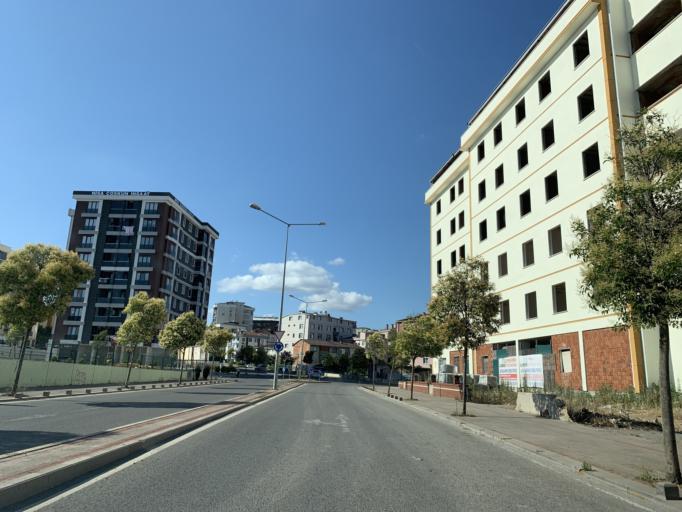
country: TR
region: Istanbul
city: Pendik
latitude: 40.8826
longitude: 29.2670
